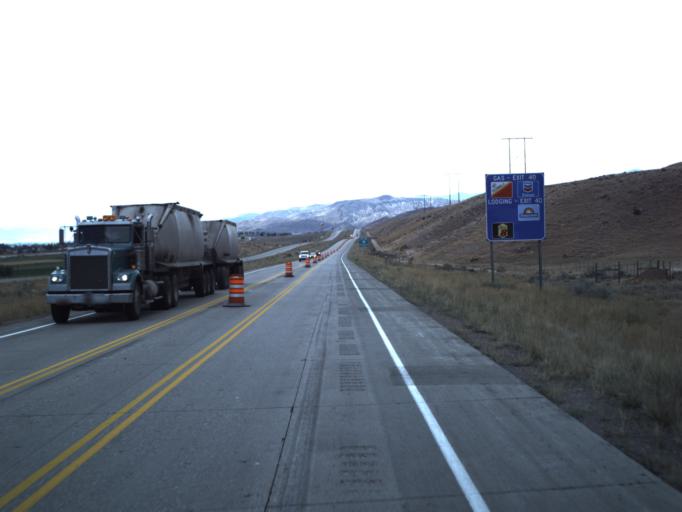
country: US
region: Utah
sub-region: Sevier County
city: Richfield
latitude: 38.8058
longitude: -112.0630
